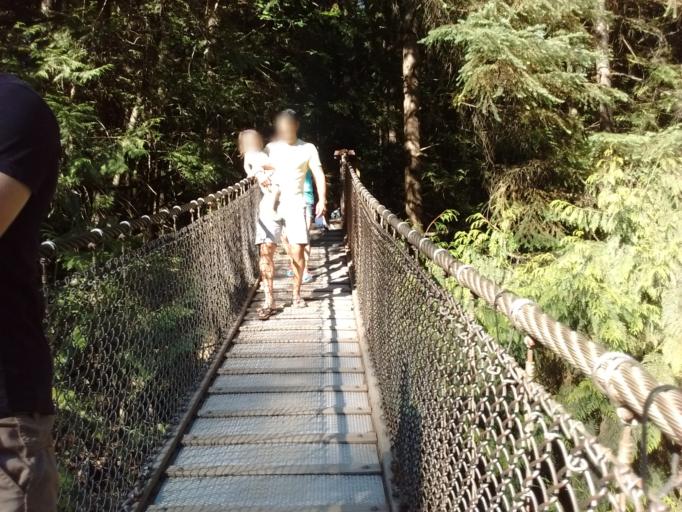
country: CA
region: British Columbia
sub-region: Fraser Valley Regional District
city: North Vancouver
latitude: 49.3439
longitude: -123.0179
